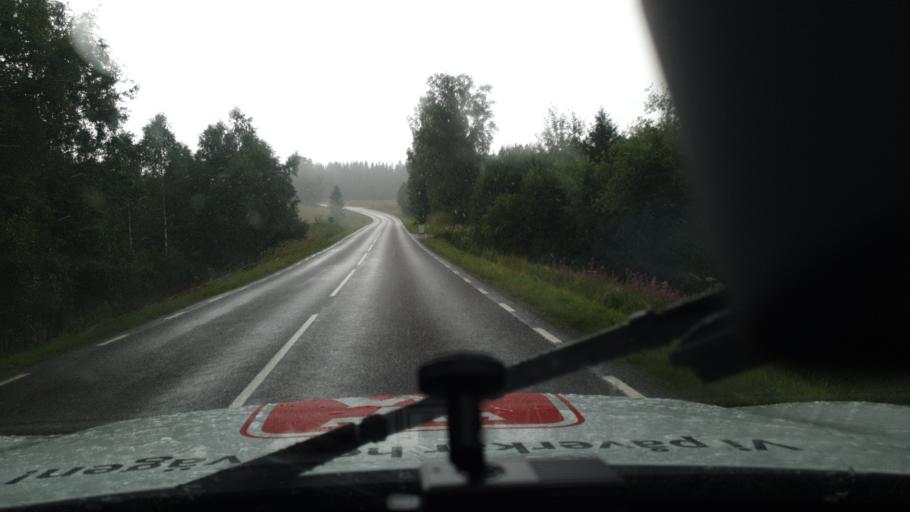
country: SE
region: Vaermland
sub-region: Sunne Kommun
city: Sunne
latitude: 59.7905
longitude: 13.0815
